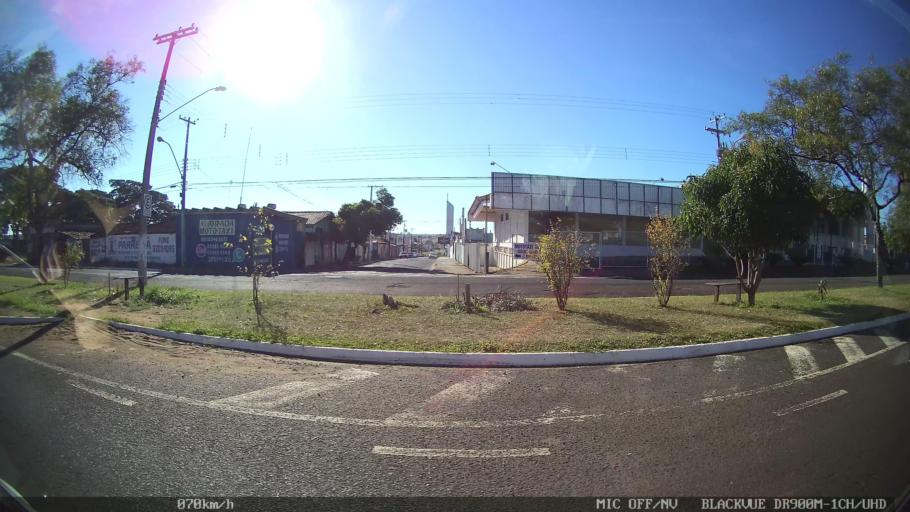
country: BR
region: Sao Paulo
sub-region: Franca
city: Franca
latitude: -20.5620
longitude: -47.3948
